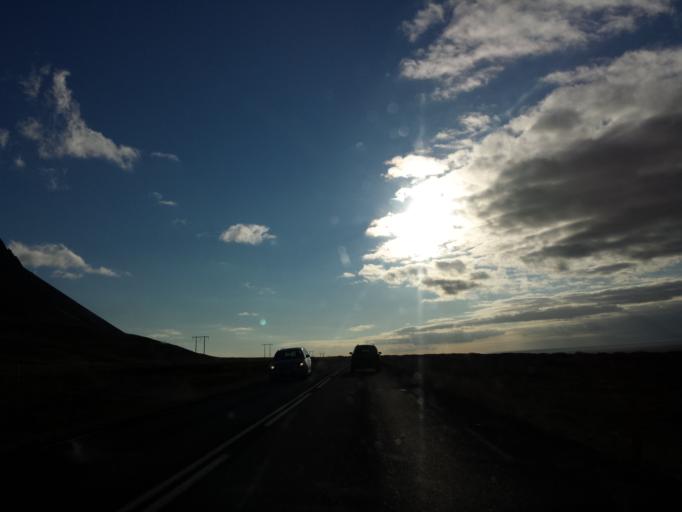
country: IS
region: West
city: Borgarnes
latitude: 64.5021
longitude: -21.9301
